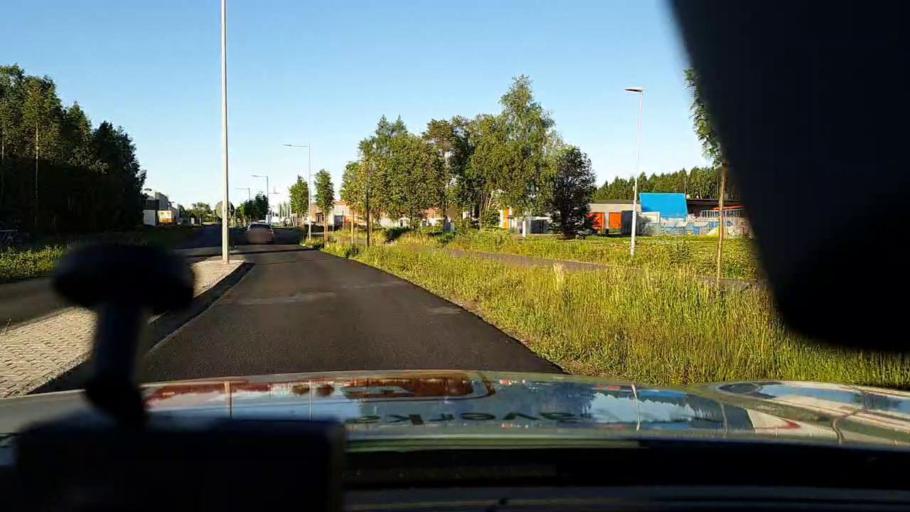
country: SE
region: Norrbotten
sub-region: Lulea Kommun
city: Bergnaset
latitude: 65.6115
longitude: 22.1232
